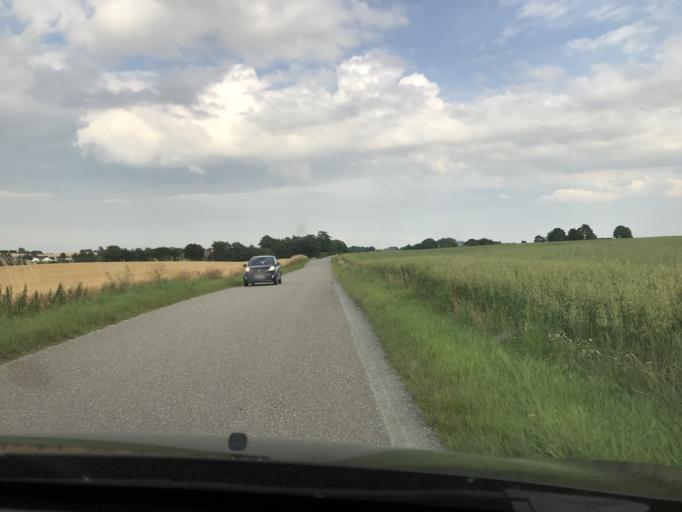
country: DK
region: South Denmark
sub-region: Vejle Kommune
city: Jelling
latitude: 55.8027
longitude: 9.4477
